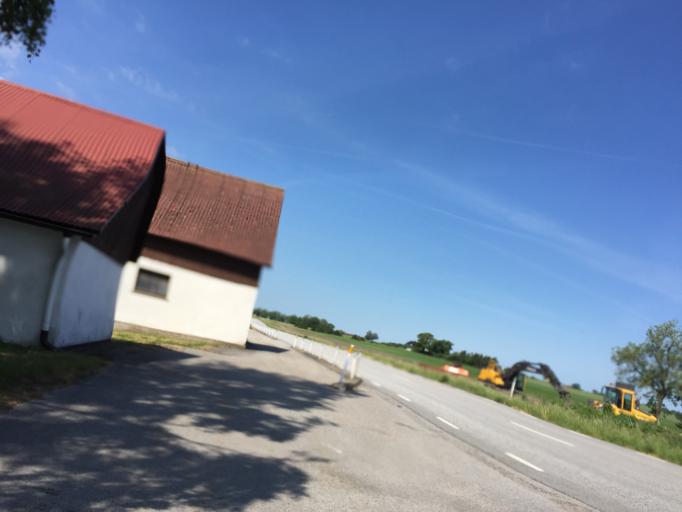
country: SE
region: Skane
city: Smygehamn
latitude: 55.3406
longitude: 13.3417
